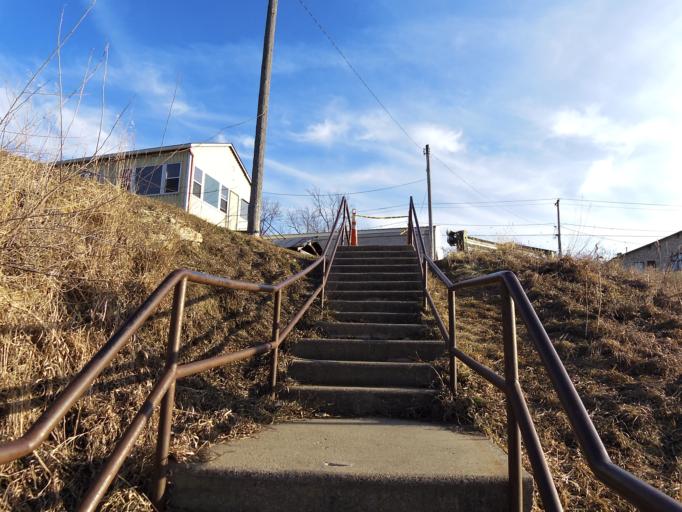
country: US
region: Minnesota
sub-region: Goodhue County
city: Cannon Falls
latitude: 44.5089
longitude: -92.9066
